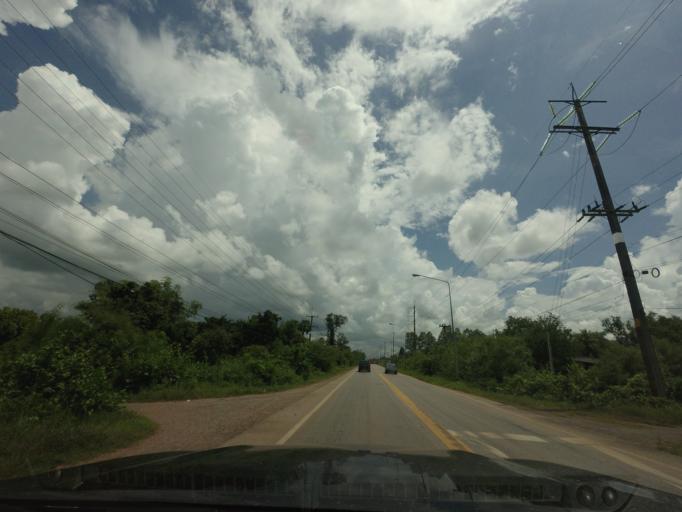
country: TH
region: Changwat Udon Thani
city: Udon Thani
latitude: 17.5300
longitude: 102.7876
